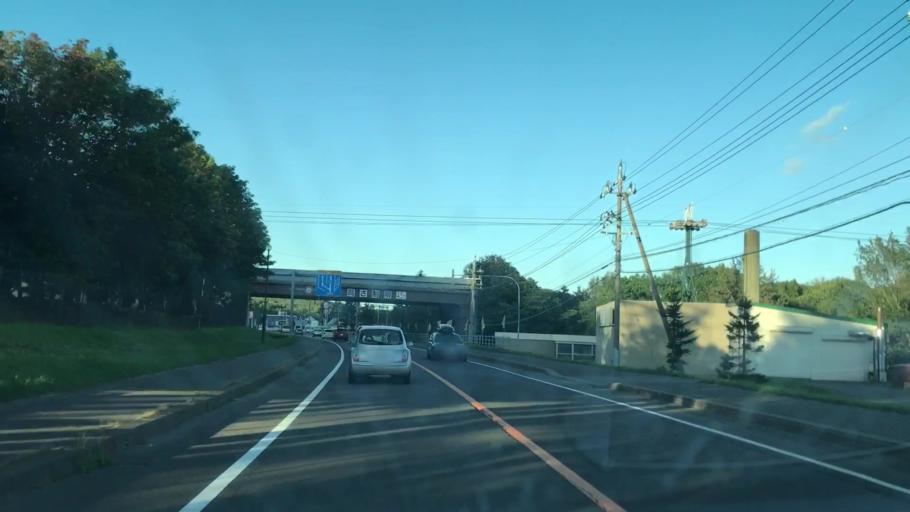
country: JP
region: Hokkaido
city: Niseko Town
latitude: 42.7479
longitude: 140.8998
